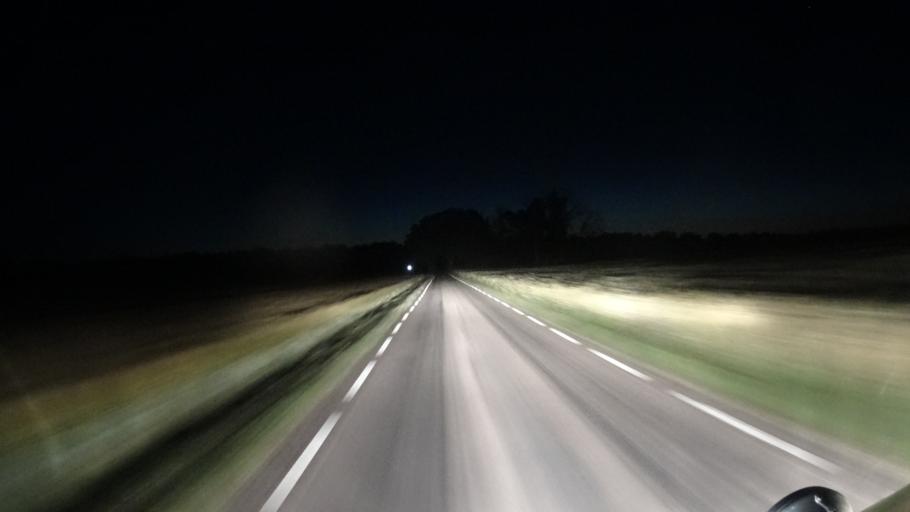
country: SE
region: OEstergoetland
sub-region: Vadstena Kommun
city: Herrestad
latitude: 58.3151
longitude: 14.8430
